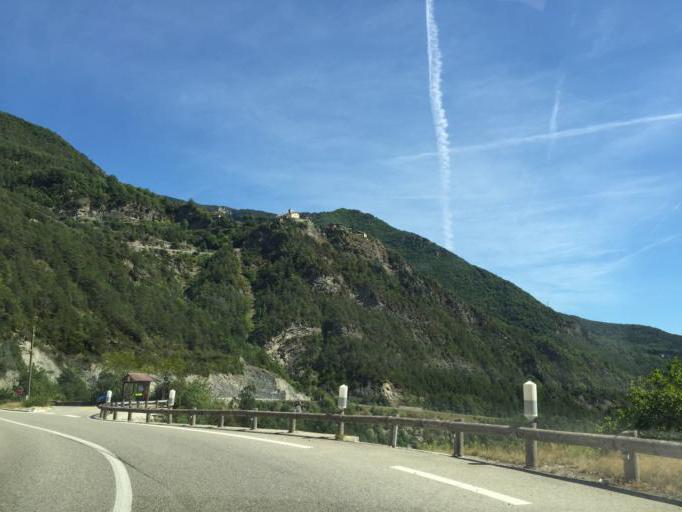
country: FR
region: Provence-Alpes-Cote d'Azur
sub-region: Departement des Alpes-Maritimes
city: Saint-Martin-Vesubie
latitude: 44.0364
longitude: 7.1281
